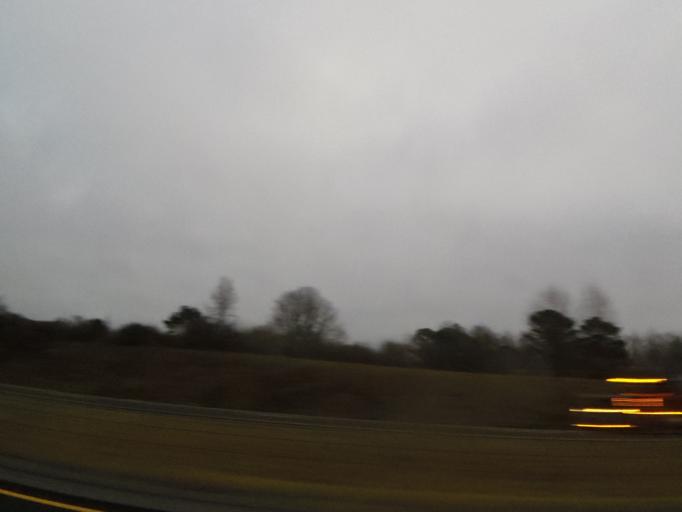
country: US
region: Alabama
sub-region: Cullman County
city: Cullman
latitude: 34.2486
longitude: -86.8879
